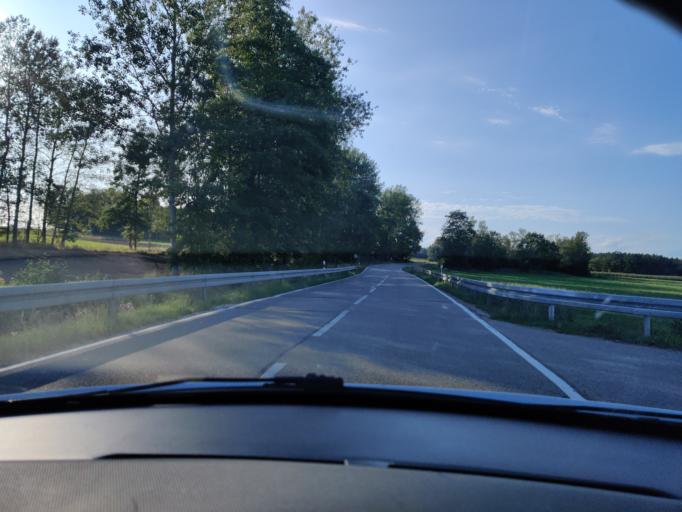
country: DE
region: Bavaria
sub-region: Upper Palatinate
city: Schwarzenfeld
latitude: 49.4002
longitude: 12.1332
